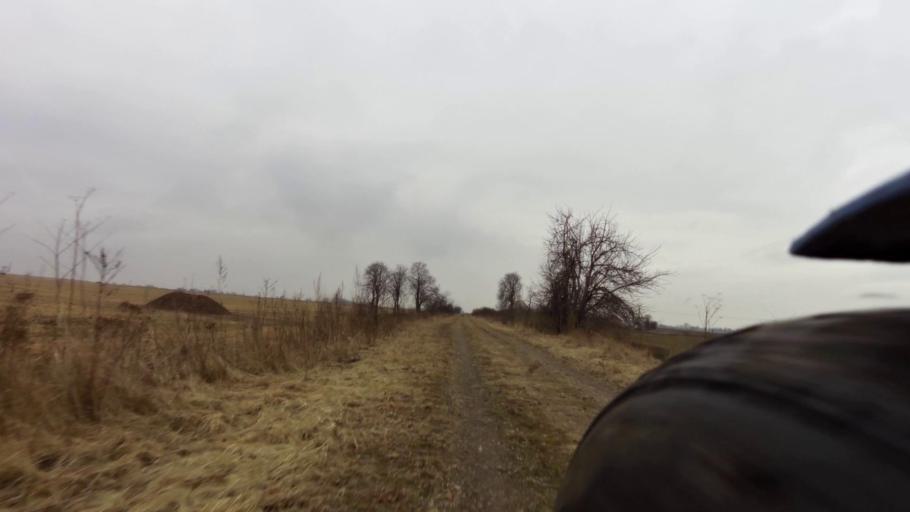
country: PL
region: West Pomeranian Voivodeship
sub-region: Powiat walecki
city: Walcz
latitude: 53.2443
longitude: 16.4721
